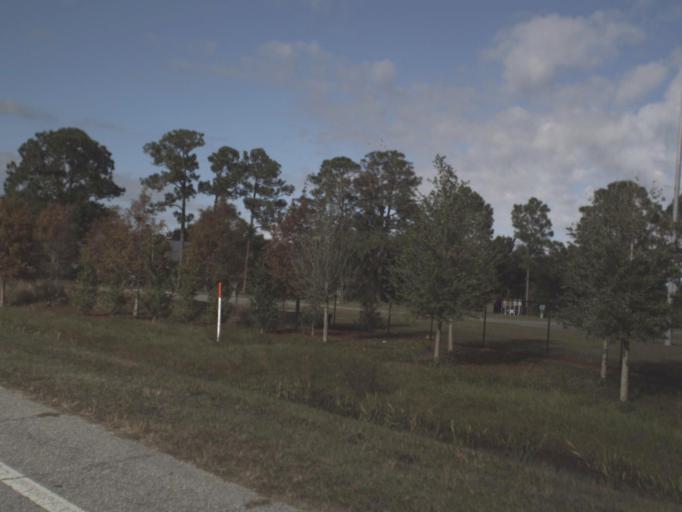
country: US
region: Florida
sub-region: Volusia County
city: Daytona Beach
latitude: 29.1809
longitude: -81.0776
